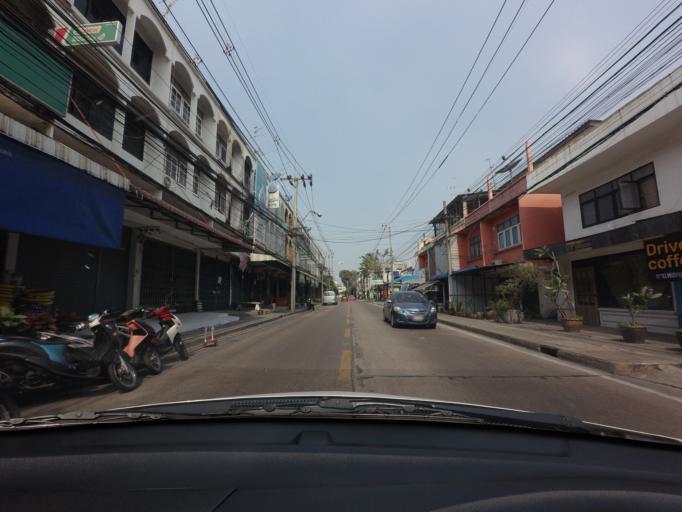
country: TH
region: Bangkok
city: Taling Chan
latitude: 13.7823
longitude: 100.4646
